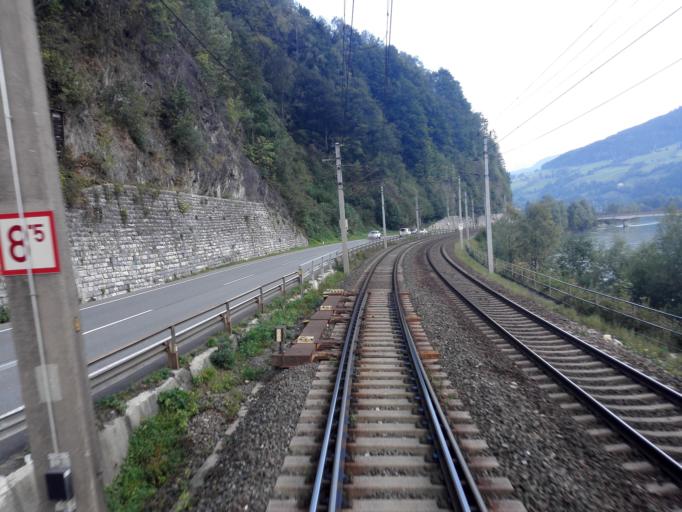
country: AT
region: Salzburg
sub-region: Politischer Bezirk Sankt Johann im Pongau
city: Bischofshofen
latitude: 47.3854
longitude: 13.2109
